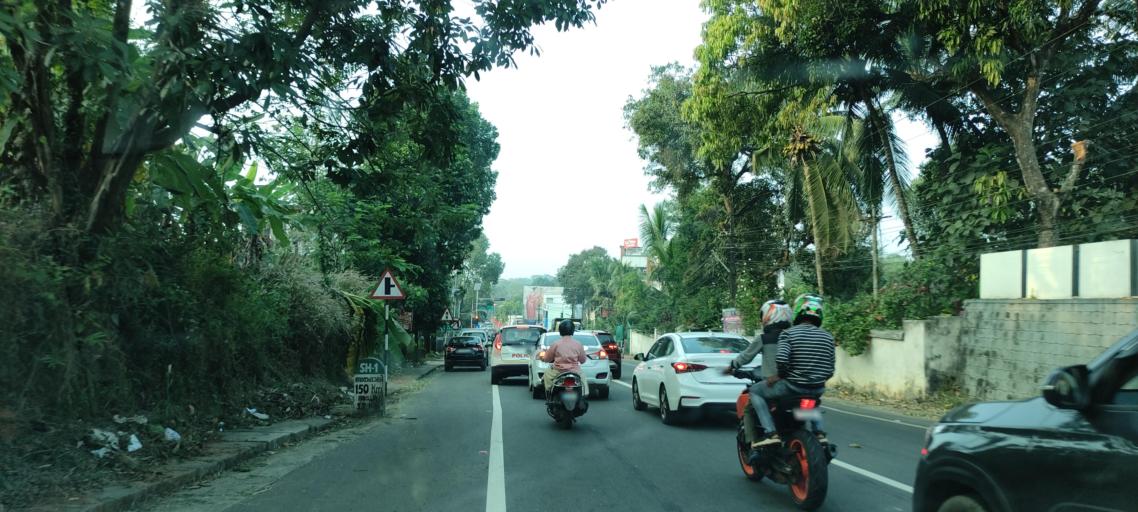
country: IN
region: Kerala
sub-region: Pattanamtitta
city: Adur
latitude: 9.1437
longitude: 76.7331
